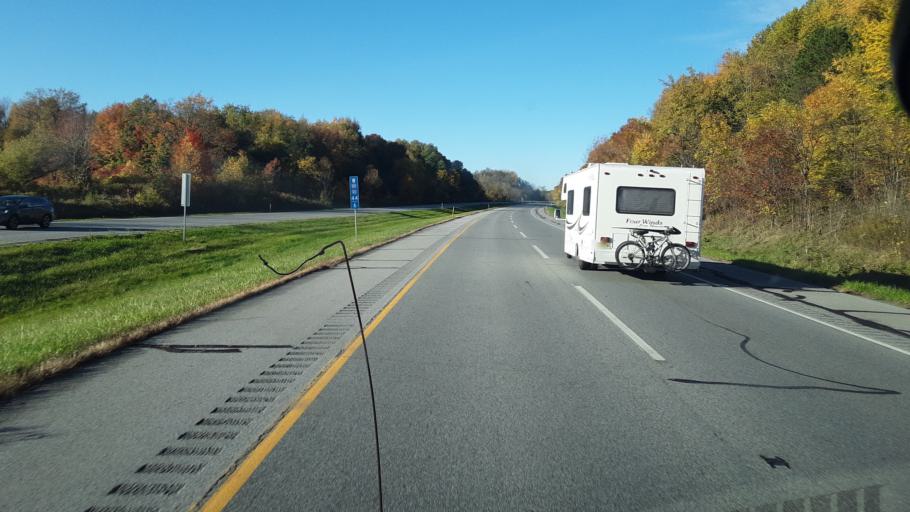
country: US
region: Indiana
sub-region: LaPorte County
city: LaPorte
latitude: 41.6252
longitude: -86.8023
